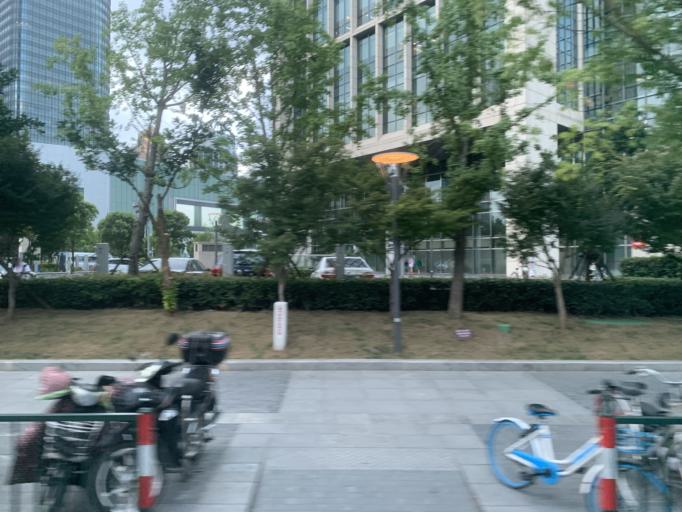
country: CN
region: Shanghai Shi
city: Pudong
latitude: 31.2309
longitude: 121.5246
